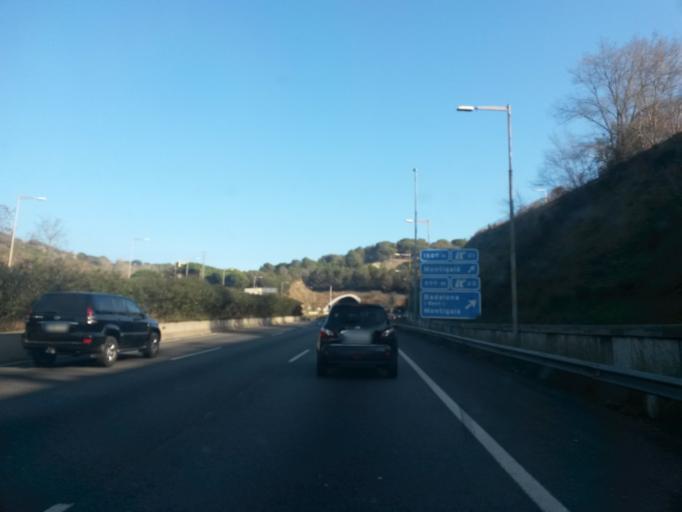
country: ES
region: Catalonia
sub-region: Provincia de Barcelona
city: Santa Coloma de Gramenet
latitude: 41.4607
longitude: 2.2150
